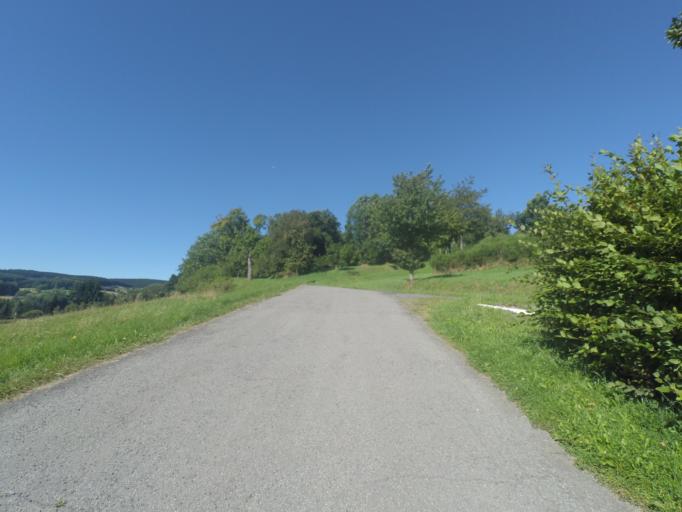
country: DE
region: Rheinland-Pfalz
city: Neroth
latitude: 50.1963
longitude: 6.7400
